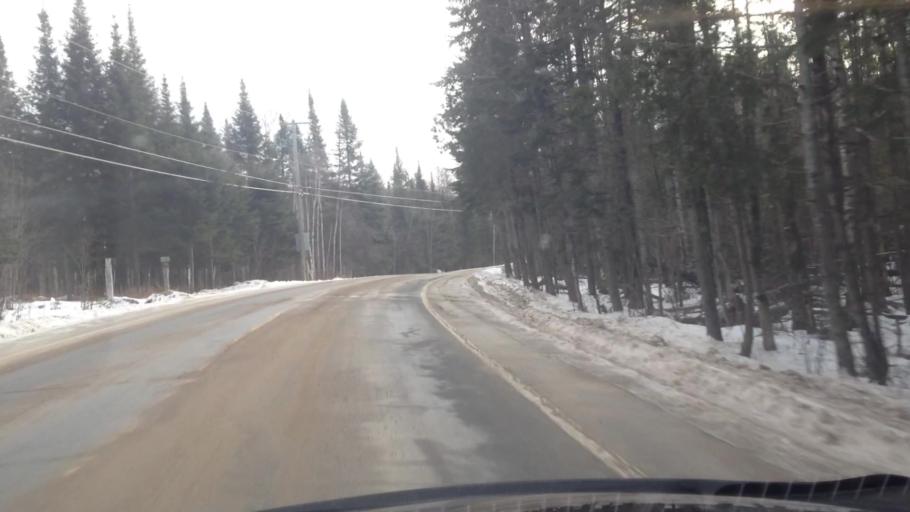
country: CA
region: Quebec
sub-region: Laurentides
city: Brownsburg-Chatham
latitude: 45.9270
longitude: -74.5423
